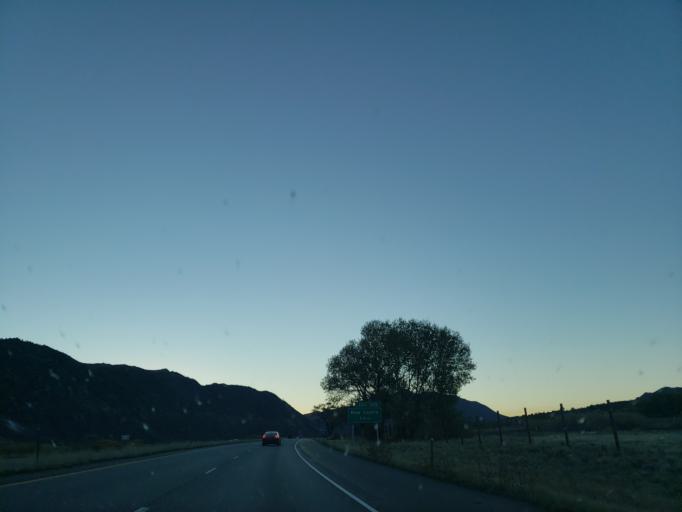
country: US
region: Colorado
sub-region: Garfield County
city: New Castle
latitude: 39.5659
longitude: -107.4935
